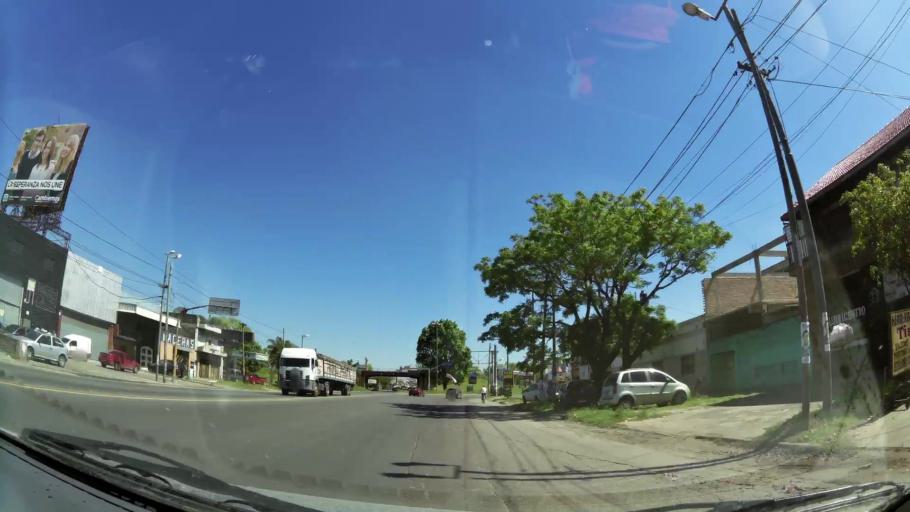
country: AR
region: Buenos Aires
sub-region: Partido de Quilmes
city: Quilmes
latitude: -34.7118
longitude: -58.3095
